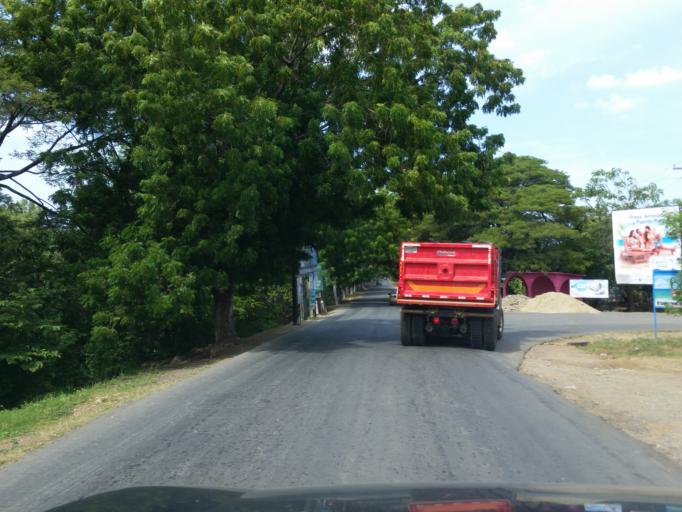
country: NI
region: Managua
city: Masachapa
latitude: 11.8092
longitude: -86.4920
